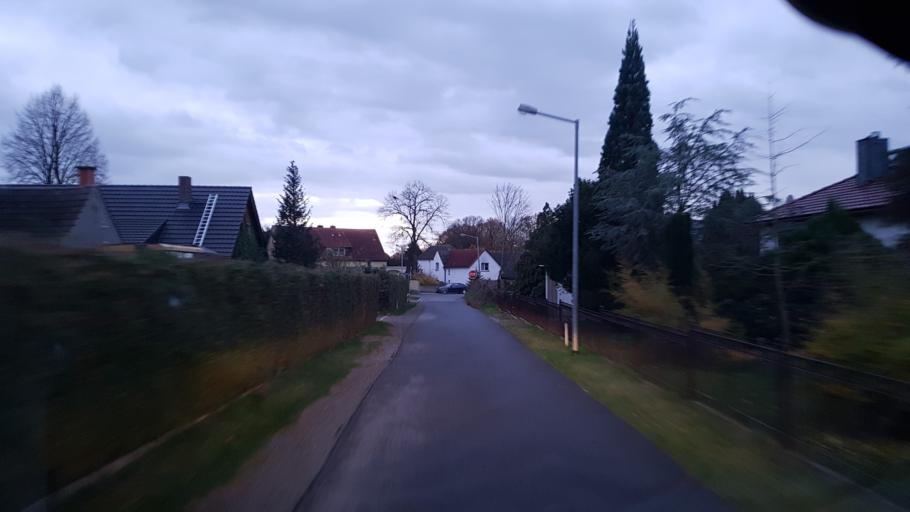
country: DE
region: Brandenburg
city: Lauchhammer
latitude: 51.5140
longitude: 13.7030
